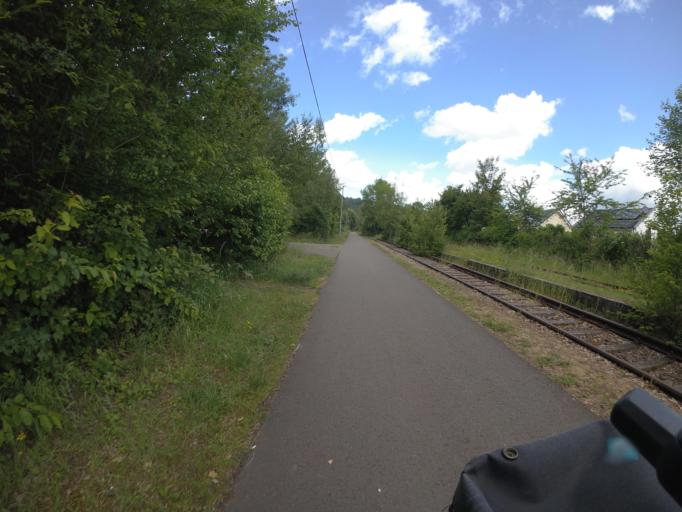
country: DE
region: Rheinland-Pfalz
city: Meisenheim
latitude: 49.7100
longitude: 7.6650
